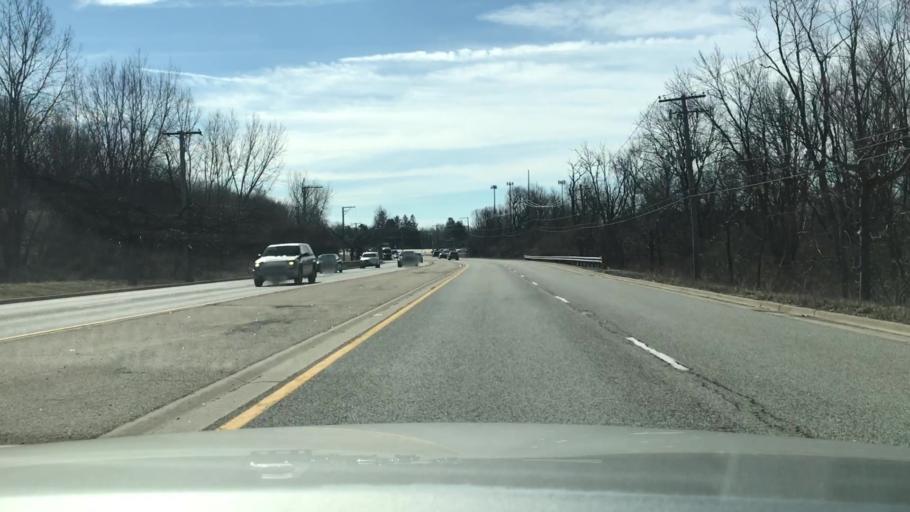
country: US
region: Illinois
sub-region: DuPage County
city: Woodridge
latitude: 41.7527
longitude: -88.0647
